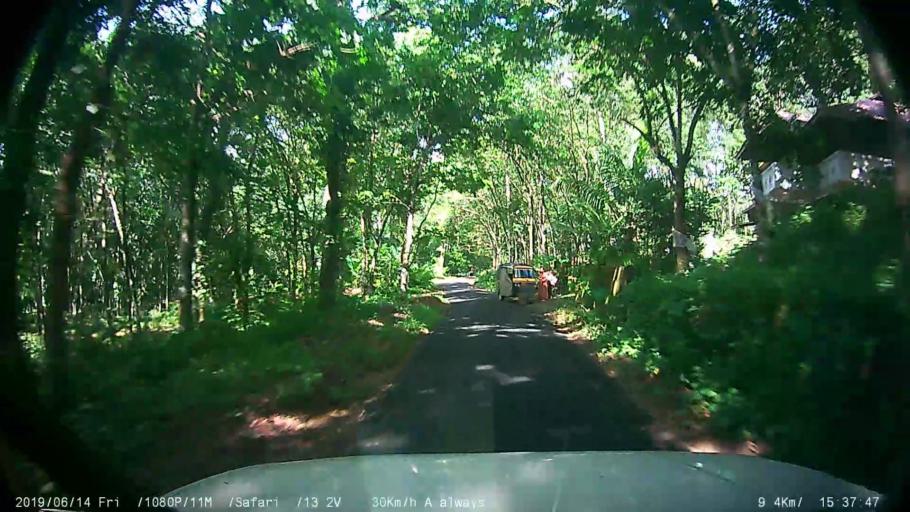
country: IN
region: Kerala
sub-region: Kottayam
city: Palackattumala
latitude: 9.7750
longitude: 76.5986
